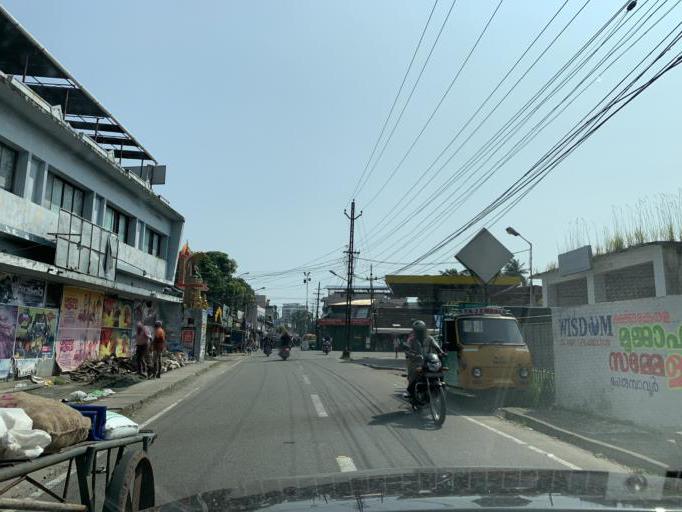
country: IN
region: Kerala
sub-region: Ernakulam
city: Cochin
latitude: 9.9525
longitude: 76.2577
